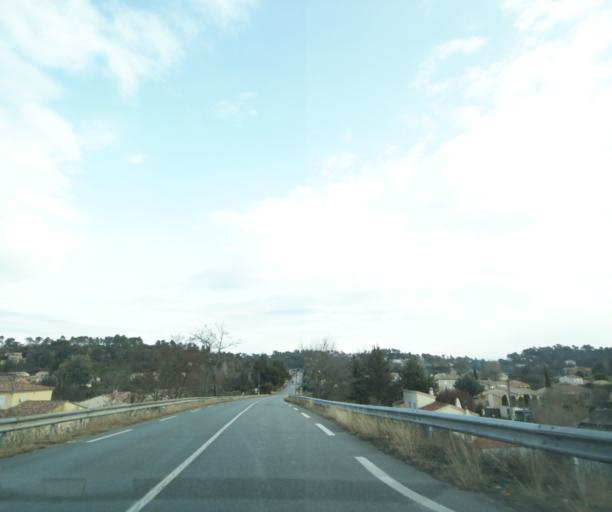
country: FR
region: Provence-Alpes-Cote d'Azur
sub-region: Departement du Var
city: Tourves
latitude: 43.4099
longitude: 5.9118
